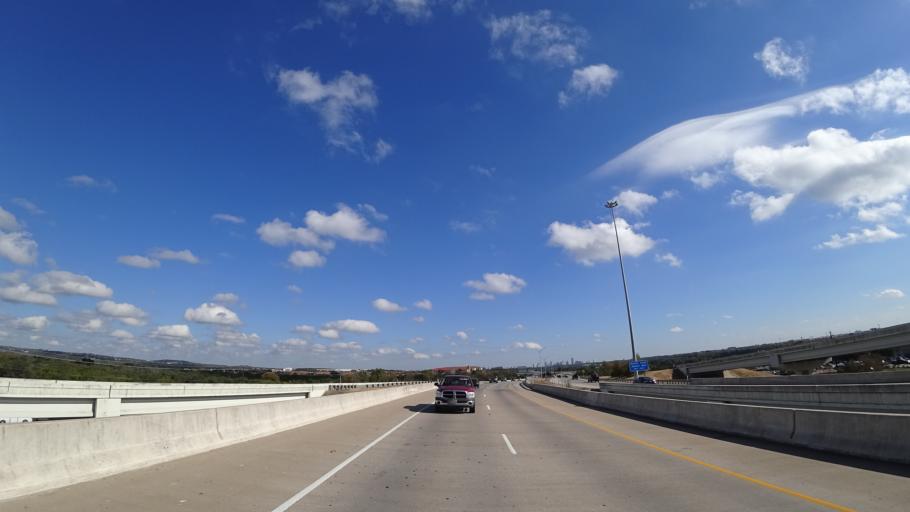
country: US
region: Texas
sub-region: Travis County
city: Rollingwood
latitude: 30.2373
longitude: -97.8230
